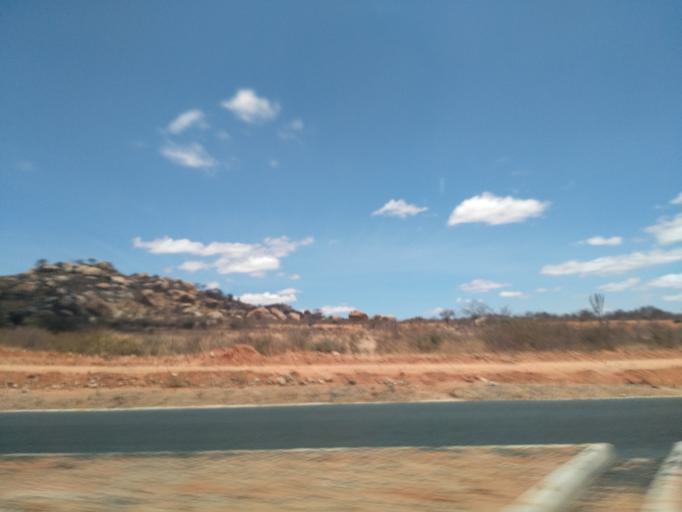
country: TZ
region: Dodoma
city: Kisasa
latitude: -6.1825
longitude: 35.8382
